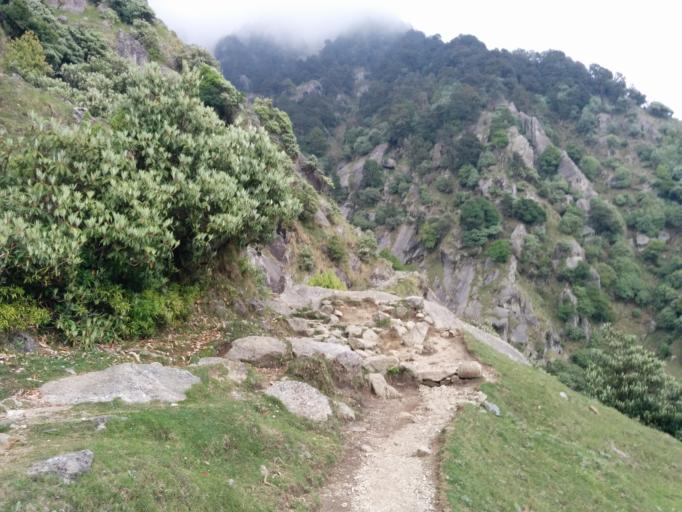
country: IN
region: Himachal Pradesh
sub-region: Kangra
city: Dharmsala
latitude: 32.2577
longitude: 76.3438
